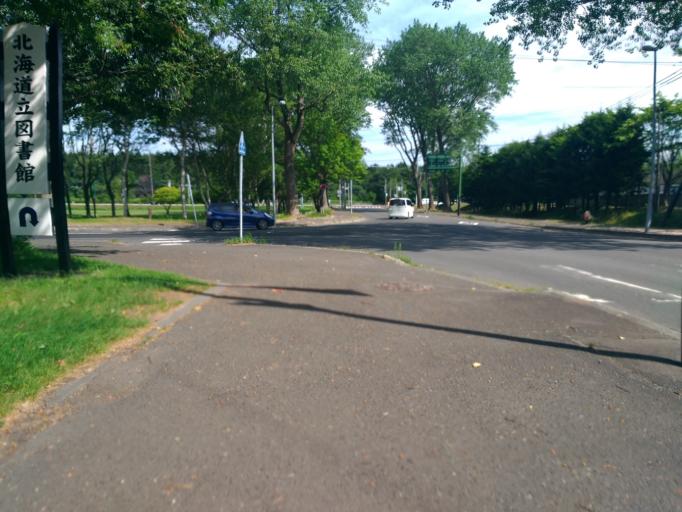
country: JP
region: Hokkaido
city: Ebetsu
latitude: 43.0716
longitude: 141.5014
